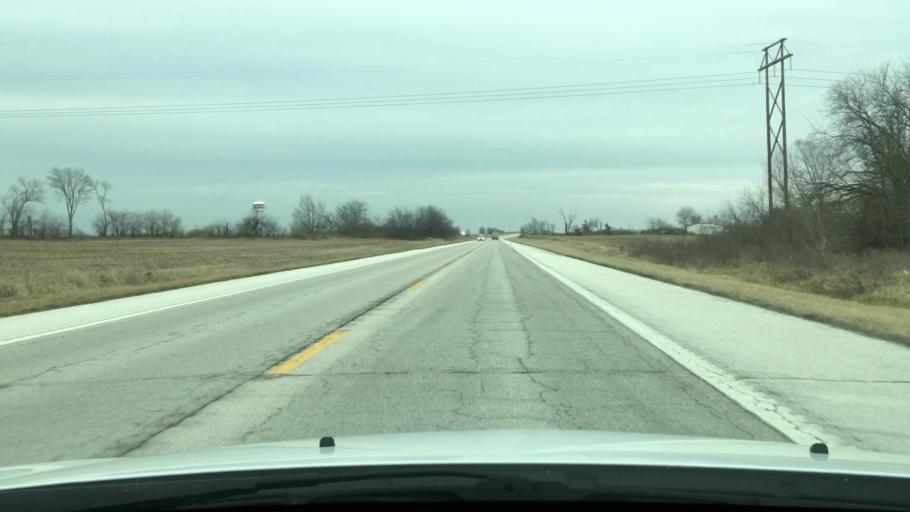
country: US
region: Missouri
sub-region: Pike County
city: Bowling Green
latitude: 39.3498
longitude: -91.2236
